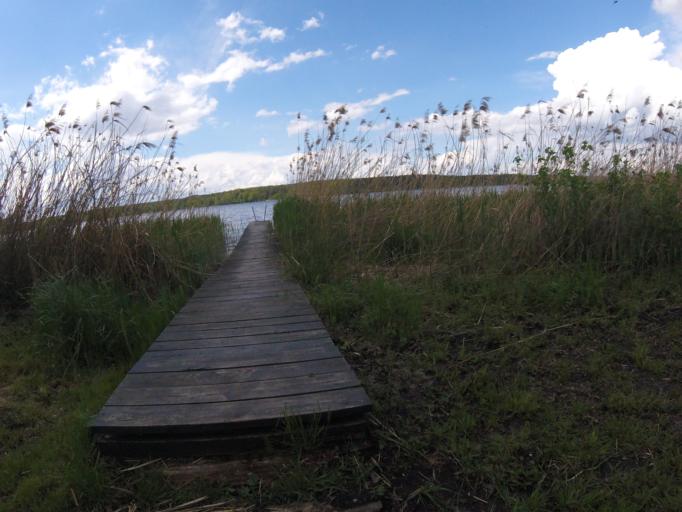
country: DE
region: Brandenburg
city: Teupitz
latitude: 52.1409
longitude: 13.6144
